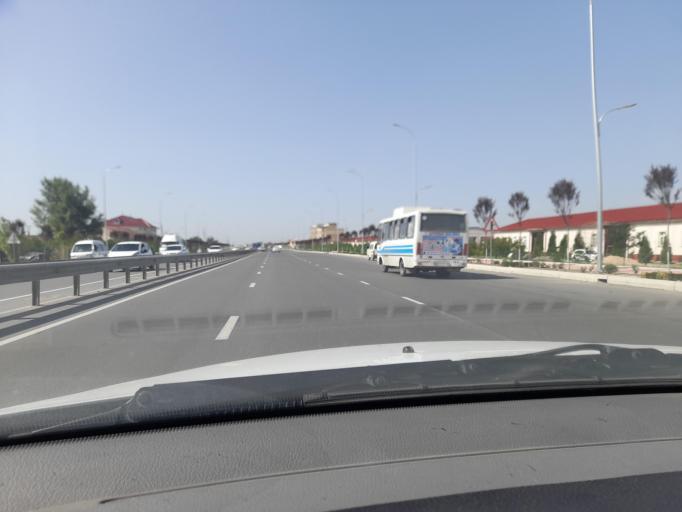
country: UZ
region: Samarqand
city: Samarqand
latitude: 39.7122
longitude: 66.9497
